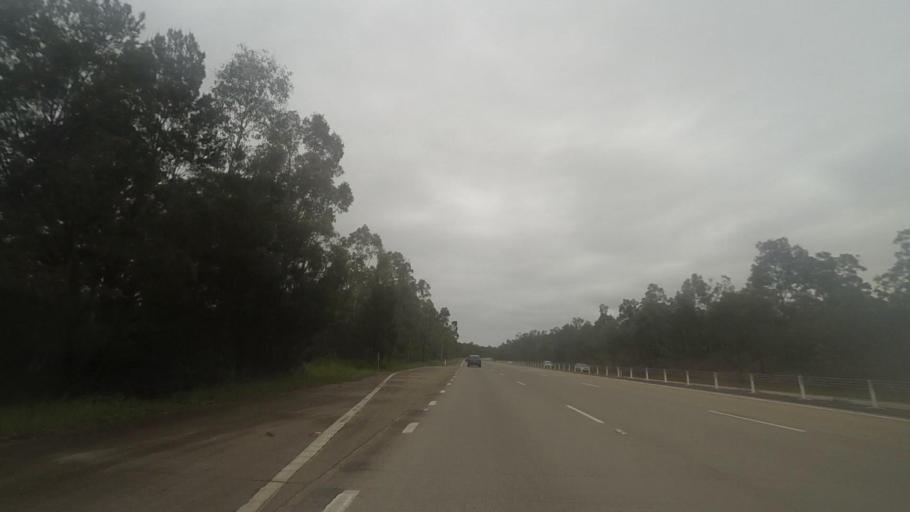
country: AU
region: New South Wales
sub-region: Port Stephens Shire
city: Medowie
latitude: -32.6889
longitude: 151.8094
